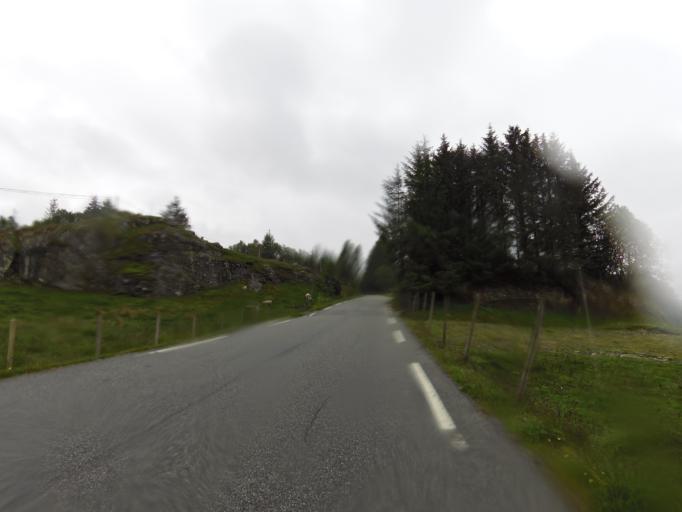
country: NO
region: Hordaland
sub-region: Sveio
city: Sveio
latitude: 59.5245
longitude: 5.2811
